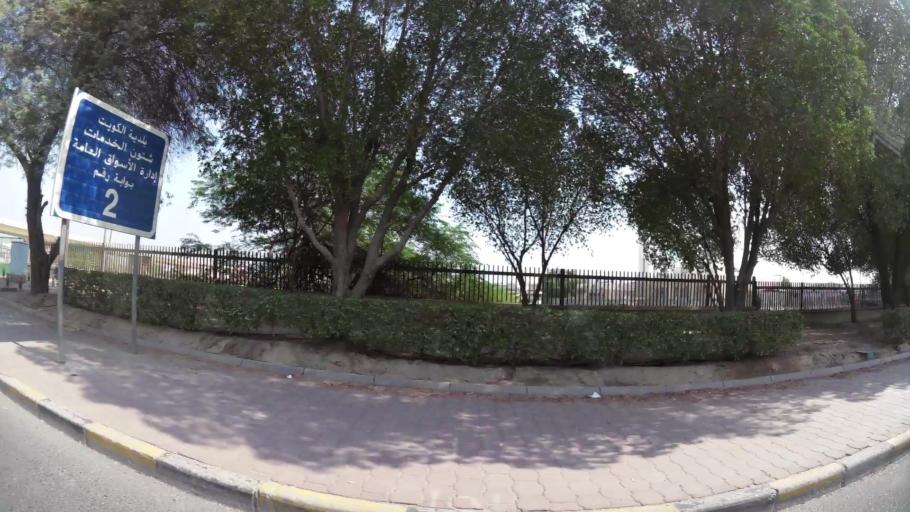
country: KW
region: Al Asimah
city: Ar Rabiyah
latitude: 29.3257
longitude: 47.9213
